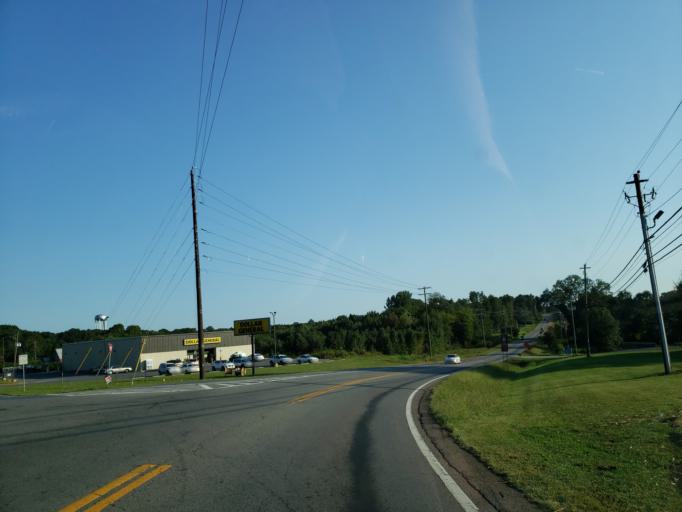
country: US
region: Georgia
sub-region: Murray County
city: Chatsworth
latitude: 34.7558
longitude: -84.8188
